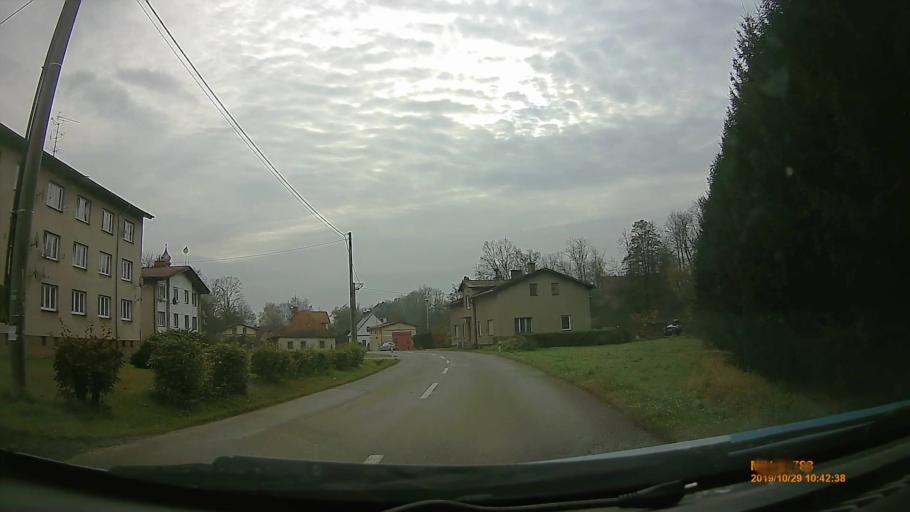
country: PL
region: Lower Silesian Voivodeship
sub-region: Powiat klodzki
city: Radkow
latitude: 50.5584
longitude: 16.3825
